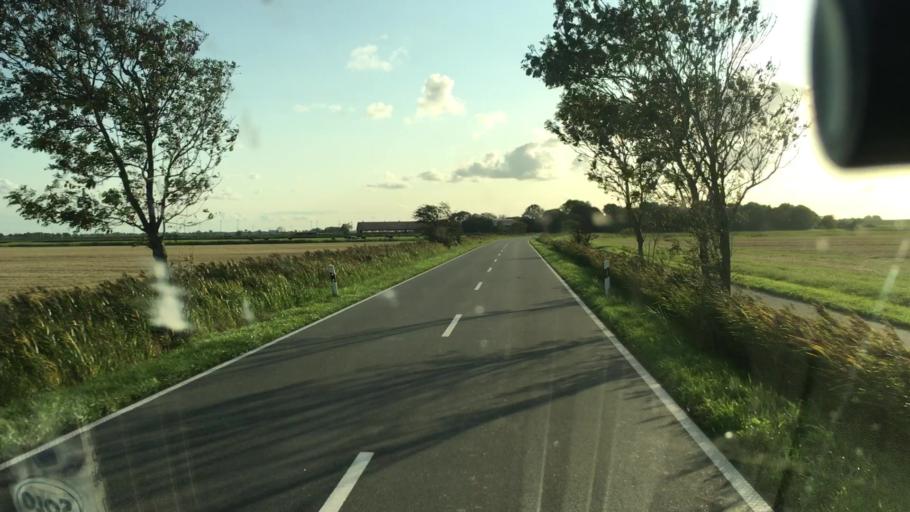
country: DE
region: Lower Saxony
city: Esens
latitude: 53.6828
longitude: 7.6087
